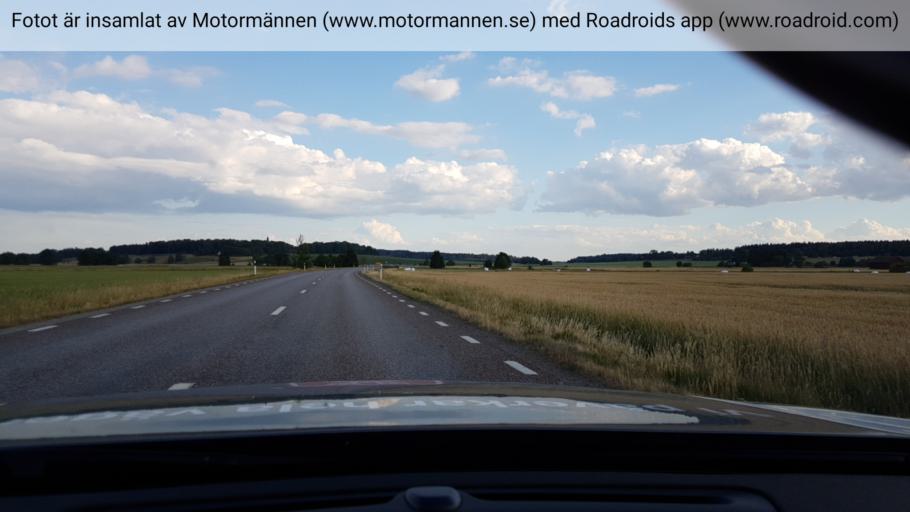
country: SE
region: Uppsala
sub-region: Heby Kommun
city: Morgongava
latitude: 59.8327
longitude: 16.9269
